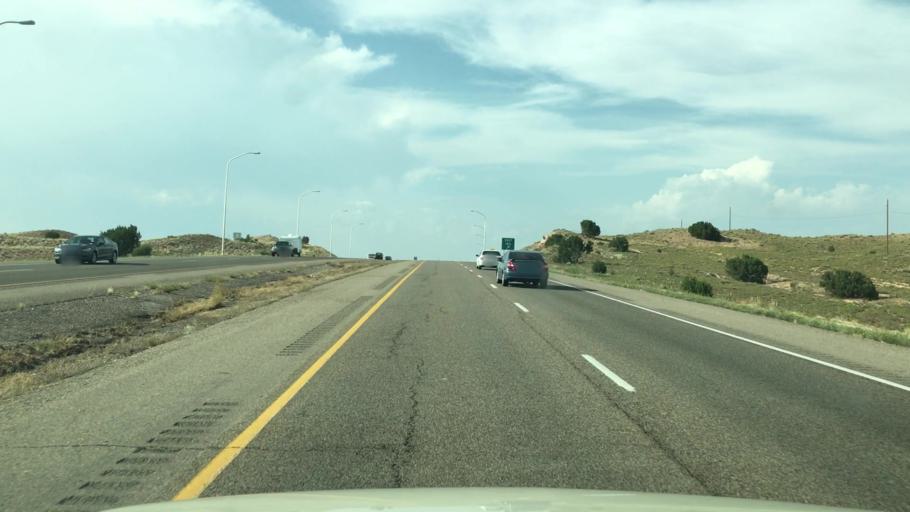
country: US
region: New Mexico
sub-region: Santa Fe County
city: Pojoaque
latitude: 35.9220
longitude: -106.0169
